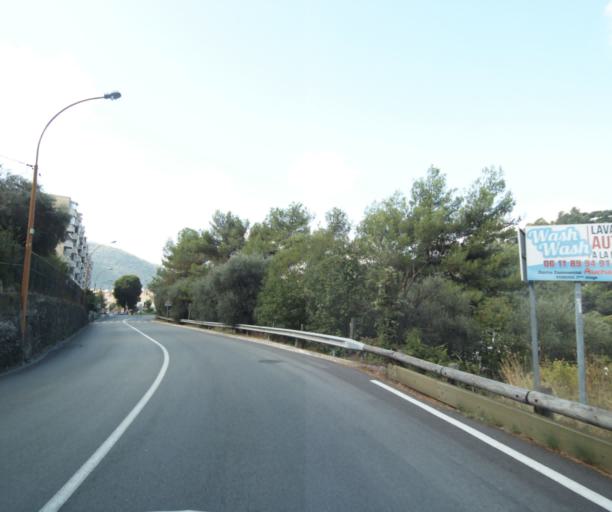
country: FR
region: Provence-Alpes-Cote d'Azur
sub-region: Departement des Alpes-Maritimes
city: La Trinite
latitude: 43.7454
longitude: 7.3156
